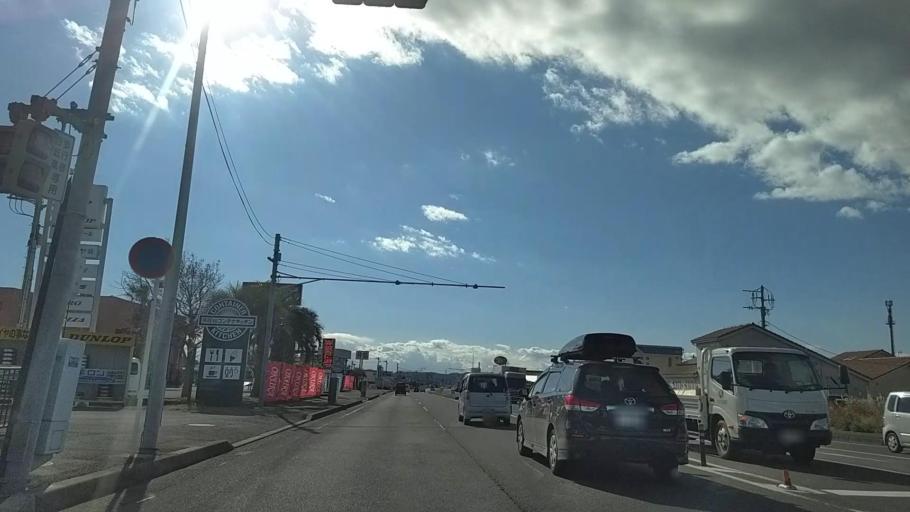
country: JP
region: Chiba
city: Tateyama
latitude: 35.0155
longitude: 139.8719
